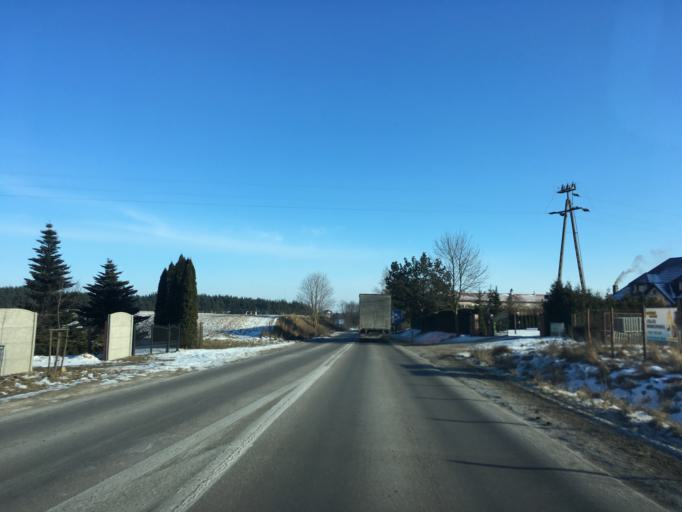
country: PL
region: Pomeranian Voivodeship
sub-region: Powiat starogardzki
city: Zblewo
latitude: 53.9366
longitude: 18.3309
